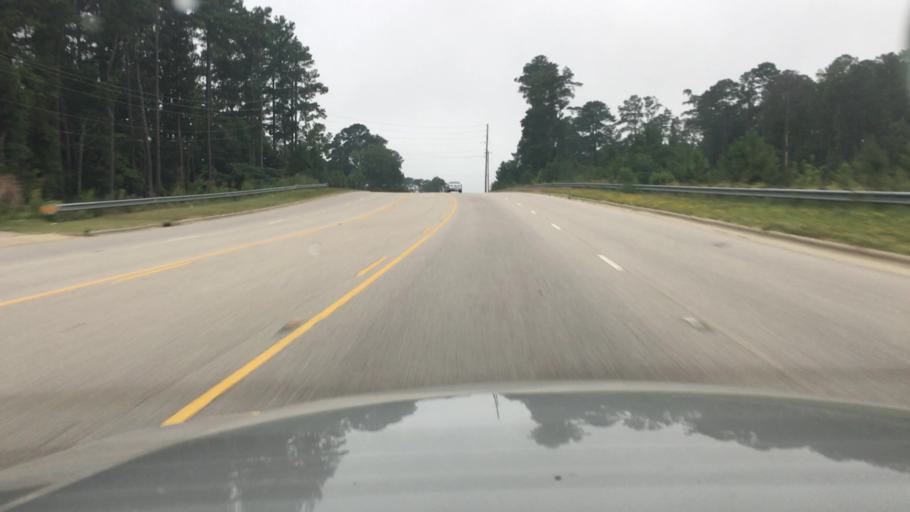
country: US
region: North Carolina
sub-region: Cumberland County
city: Fayetteville
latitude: 35.0100
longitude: -78.8763
